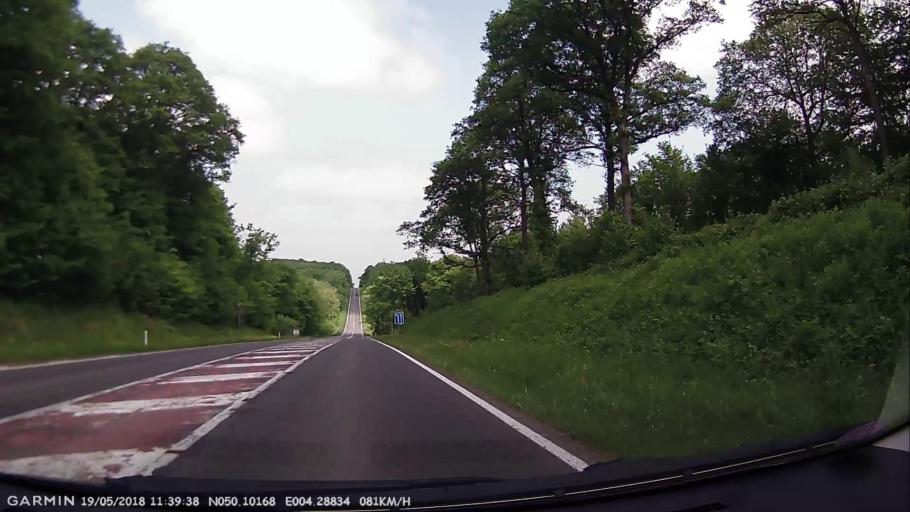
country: BE
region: Wallonia
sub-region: Province du Hainaut
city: Chimay
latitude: 50.1020
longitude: 4.2882
